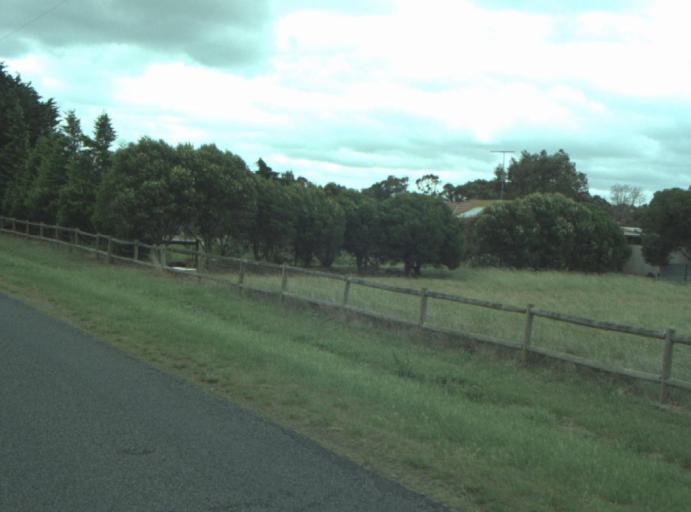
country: AU
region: Victoria
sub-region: Greater Geelong
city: Bell Post Hill
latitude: -38.0684
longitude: 144.3114
